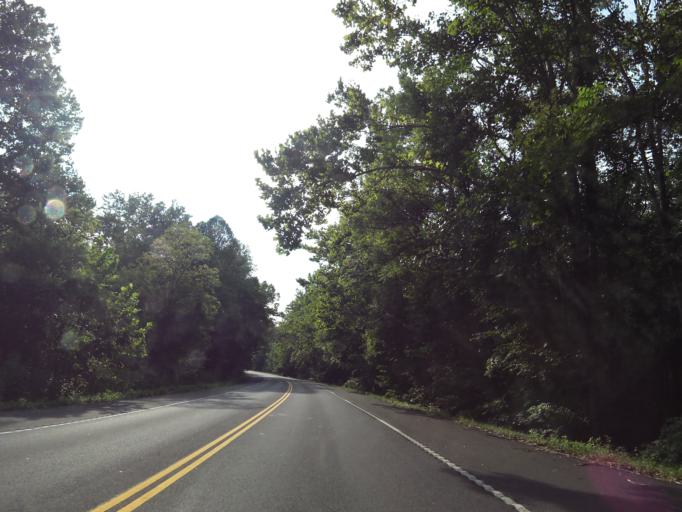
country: US
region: Tennessee
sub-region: Roane County
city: Oliver Springs
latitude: 35.9443
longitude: -84.3462
